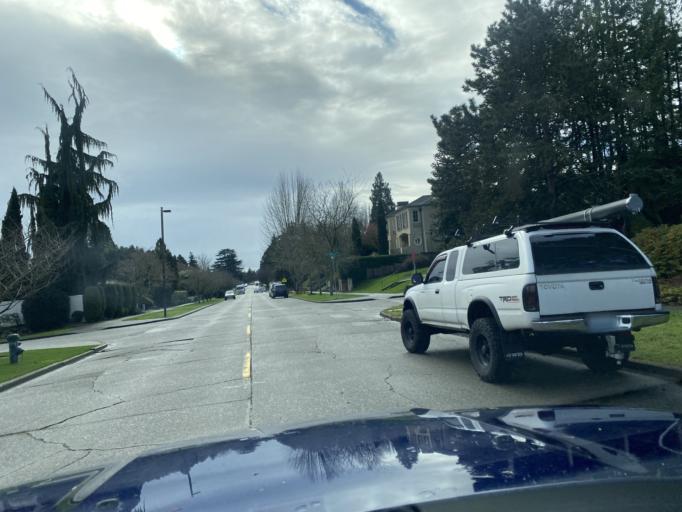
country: US
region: Washington
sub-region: King County
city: Medina
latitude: 47.6325
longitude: -122.2814
